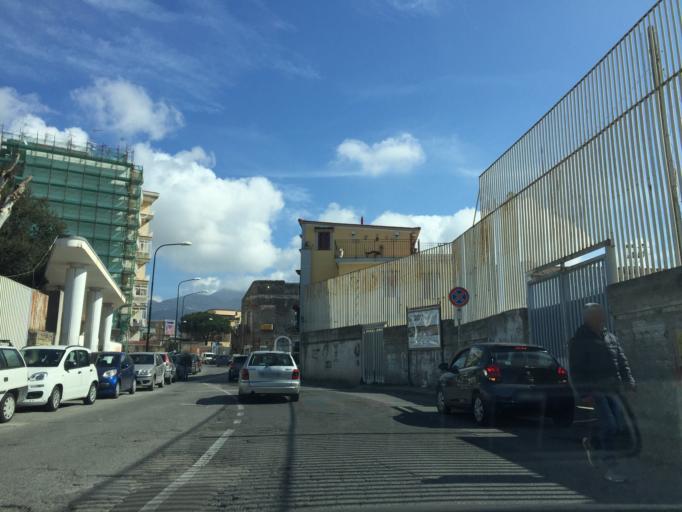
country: IT
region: Campania
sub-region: Provincia di Napoli
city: Portici
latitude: 40.8245
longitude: 14.3351
